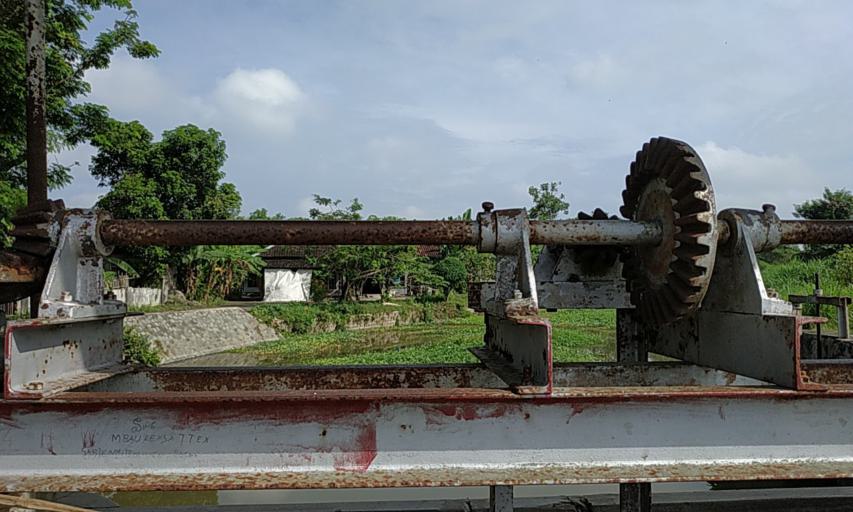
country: ID
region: Central Java
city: Trucuk
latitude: -7.7657
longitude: 110.6839
